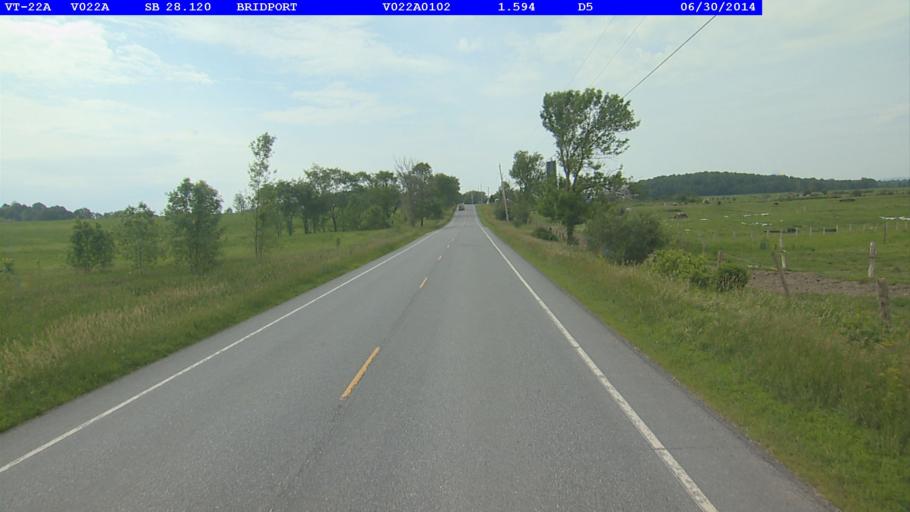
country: US
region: Vermont
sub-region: Addison County
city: Middlebury (village)
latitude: 43.9632
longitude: -73.3090
